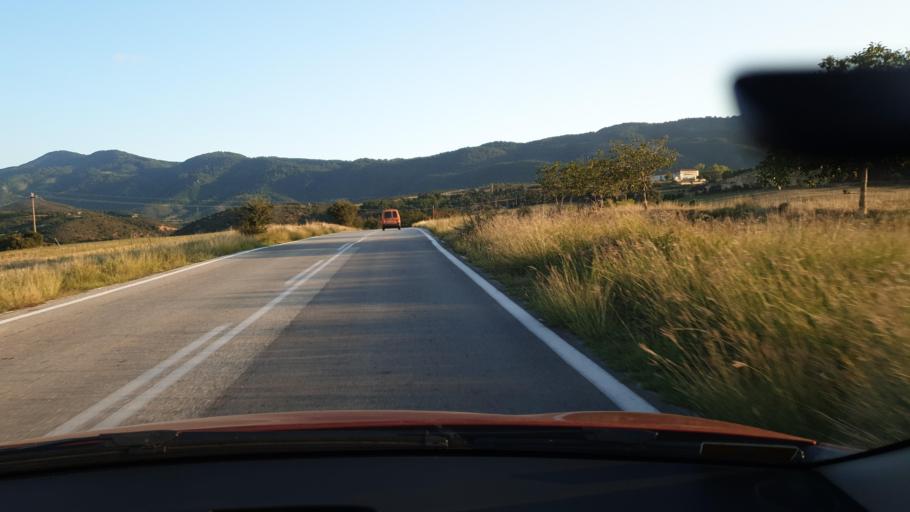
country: GR
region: Central Macedonia
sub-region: Nomos Thessalonikis
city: Nea Apollonia
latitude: 40.5105
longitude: 23.4742
